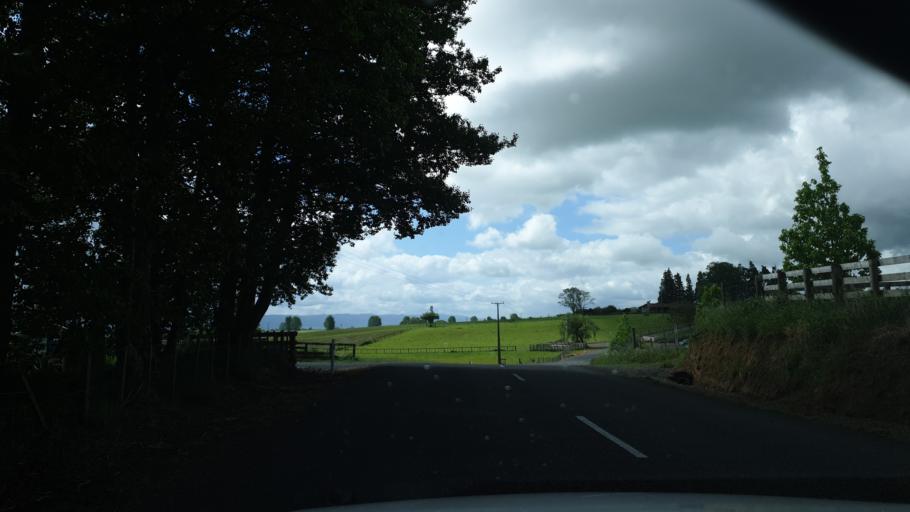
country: NZ
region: Waikato
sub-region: Matamata-Piako District
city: Matamata
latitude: -37.8354
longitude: 175.7281
